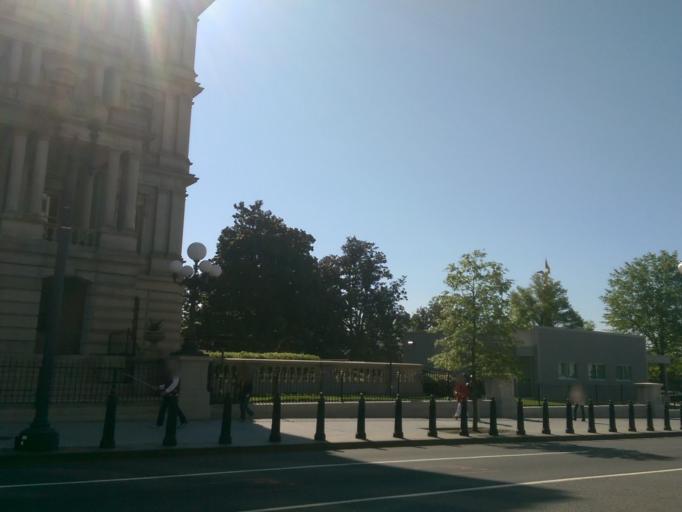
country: US
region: Washington, D.C.
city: Washington, D.C.
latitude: 38.8972
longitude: -77.0394
